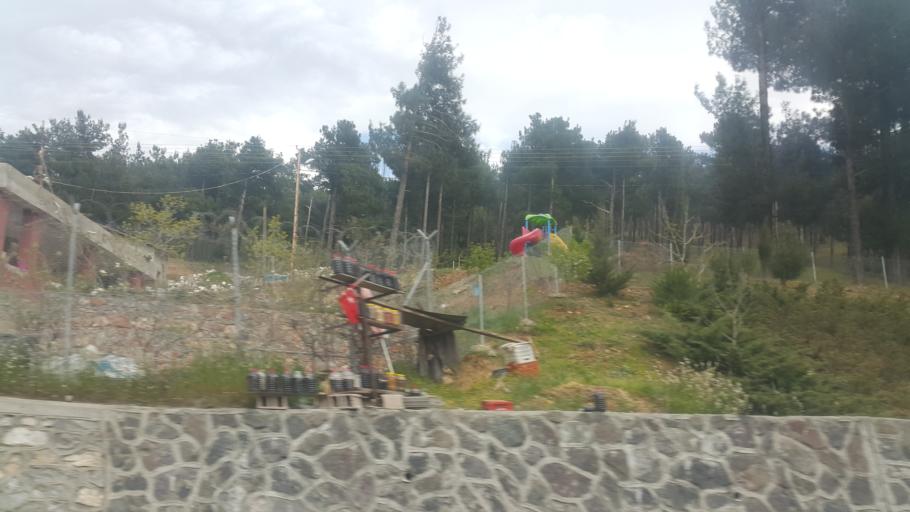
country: TR
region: Adana
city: Pozanti
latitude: 37.4234
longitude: 34.8768
